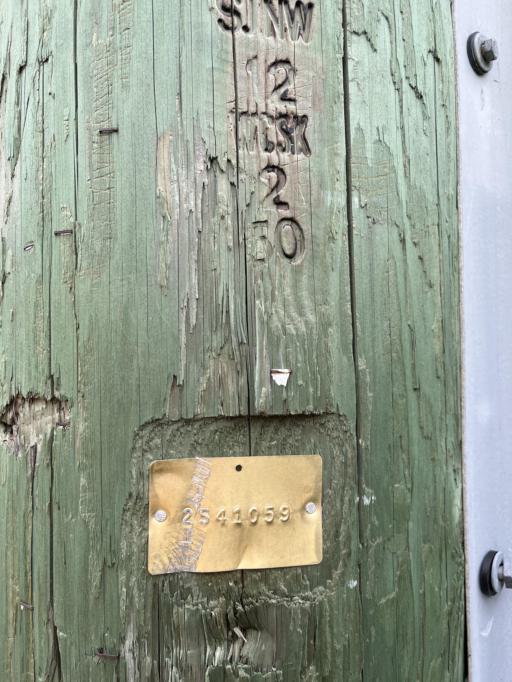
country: CA
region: British Columbia
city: Ladner
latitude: 49.0906
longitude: -123.0758
